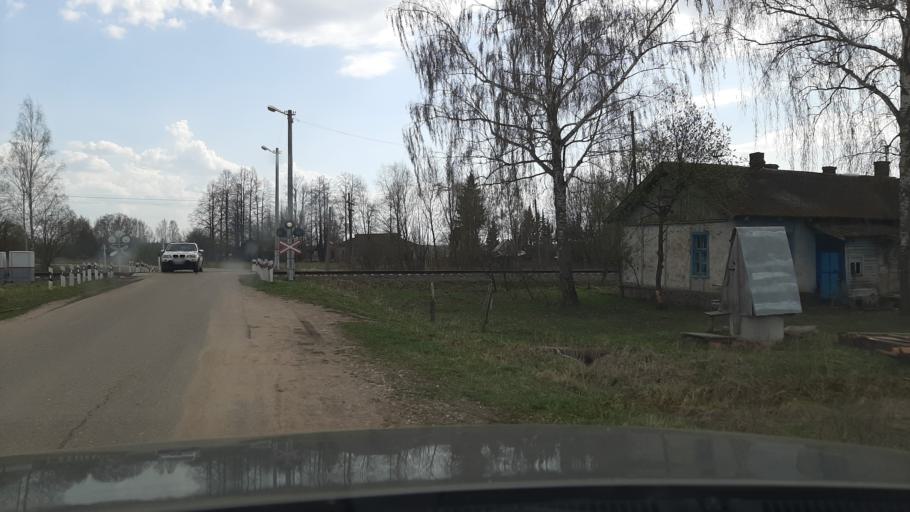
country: RU
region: Ivanovo
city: Furmanov
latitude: 57.3030
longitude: 41.1620
